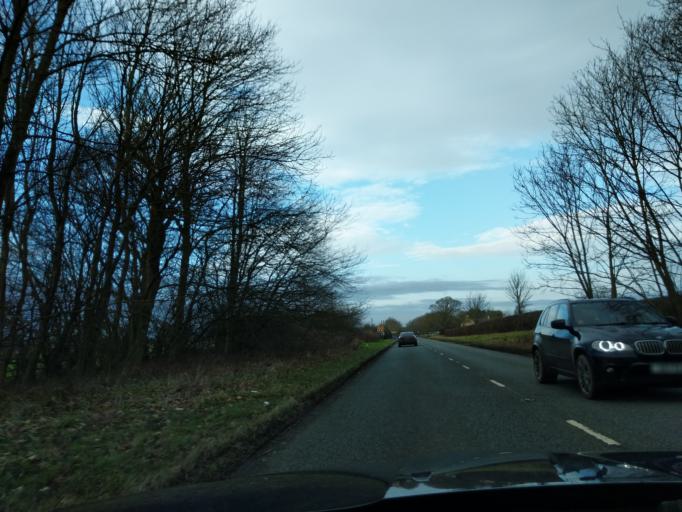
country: GB
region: England
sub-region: Northumberland
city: Darras Hall
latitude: 55.0742
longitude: -1.7966
